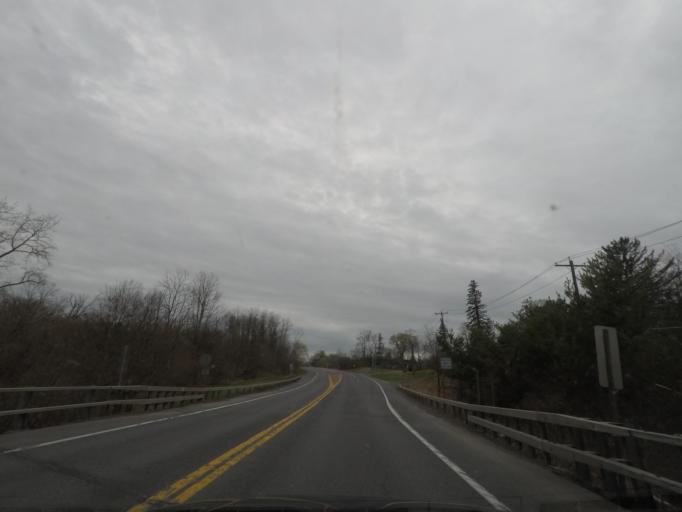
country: US
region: New York
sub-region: Albany County
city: Delmar
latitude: 42.5600
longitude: -73.8078
